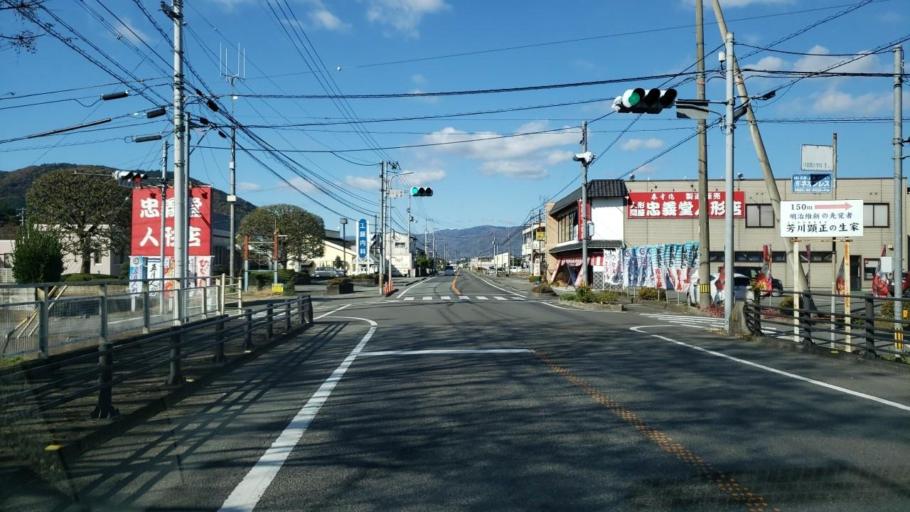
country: JP
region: Tokushima
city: Wakimachi
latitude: 34.0584
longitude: 134.2213
